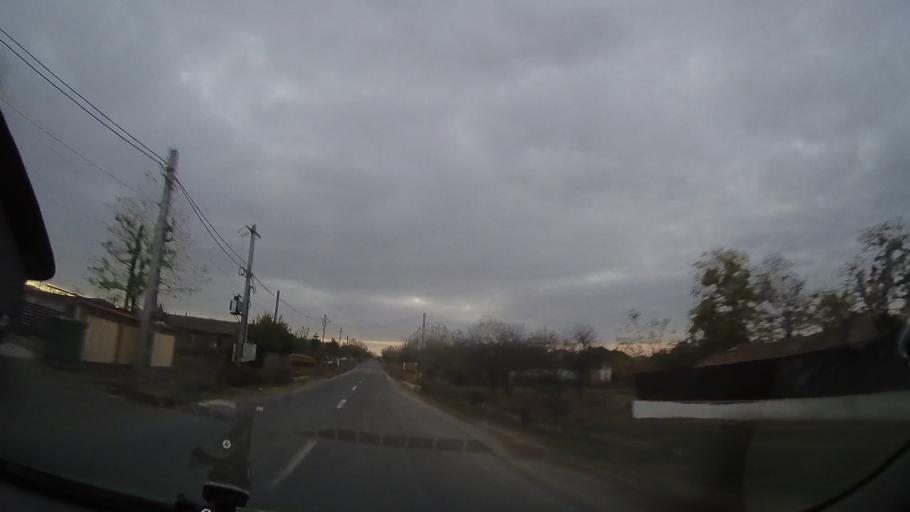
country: RO
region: Tulcea
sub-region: Comuna Mihai Bravu
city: Turda
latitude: 44.9737
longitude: 28.6247
